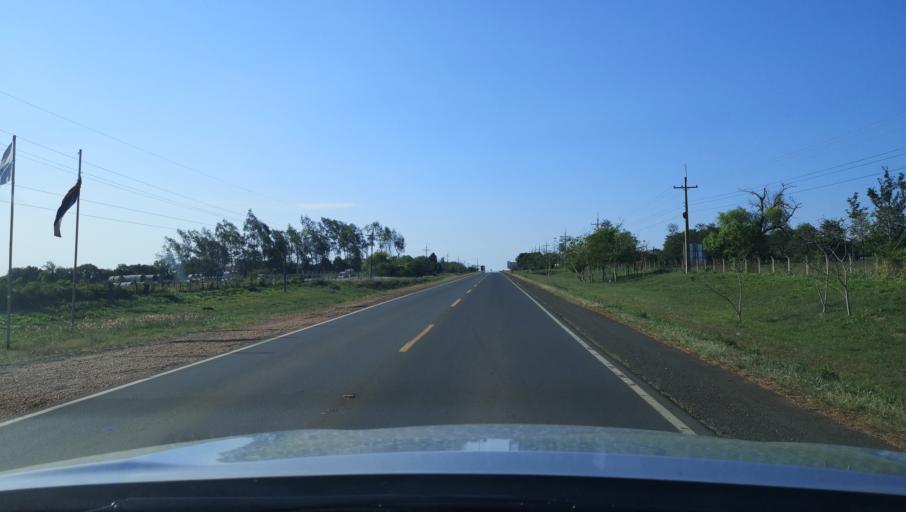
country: PY
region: Misiones
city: Santa Maria
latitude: -26.8589
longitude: -57.0347
